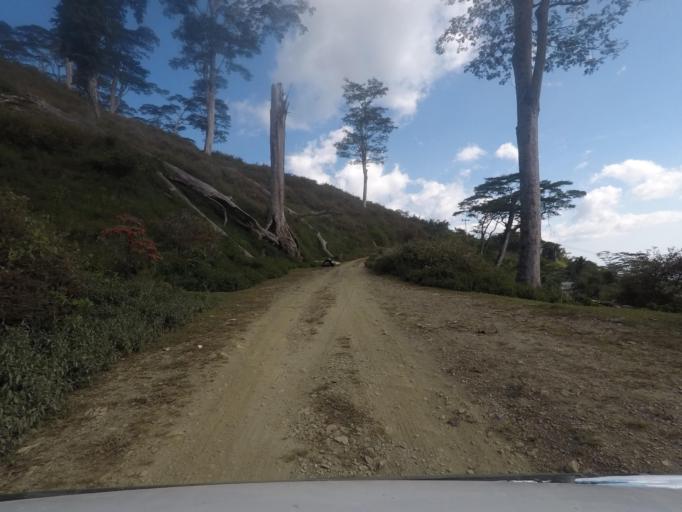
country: TL
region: Ermera
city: Gleno
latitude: -8.7490
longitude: 125.3261
